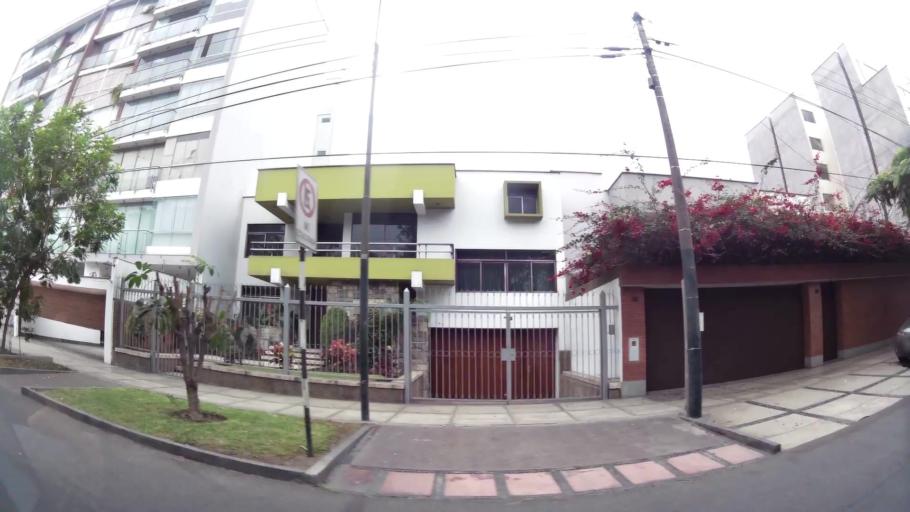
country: PE
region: Lima
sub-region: Lima
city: San Luis
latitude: -12.0923
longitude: -77.0172
